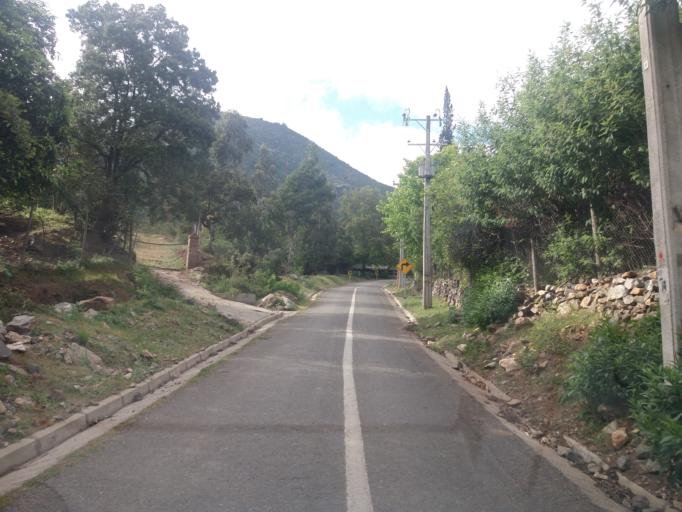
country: CL
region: Valparaiso
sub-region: Provincia de Marga Marga
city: Limache
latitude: -33.0690
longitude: -71.0633
